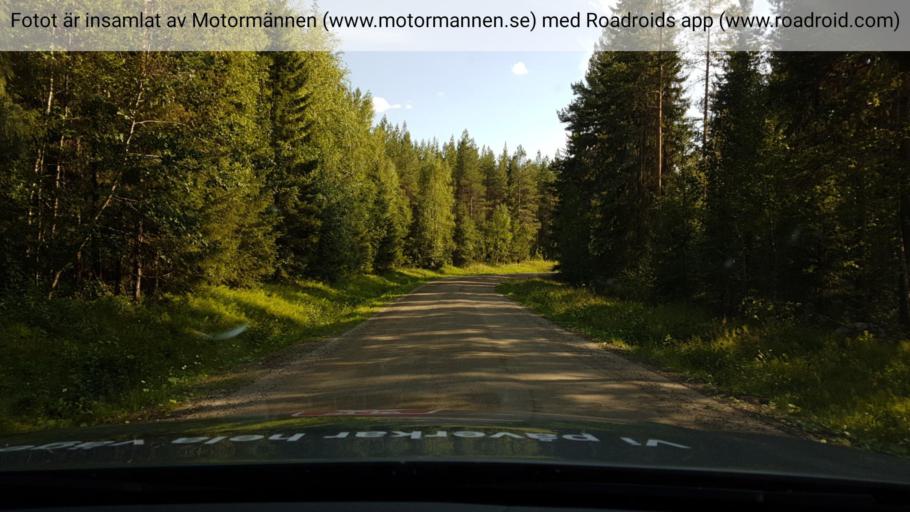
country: SE
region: Vaesternorrland
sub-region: Solleftea Kommun
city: As
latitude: 63.7407
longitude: 16.2505
